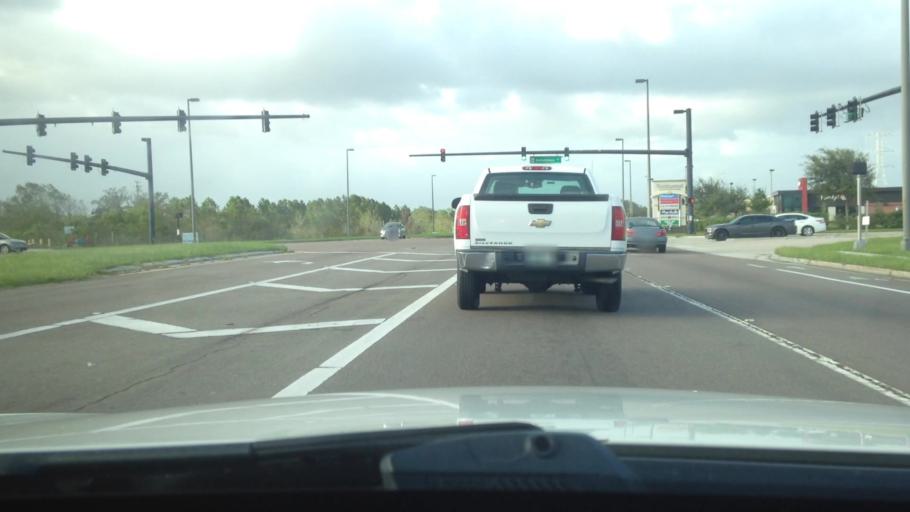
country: US
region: Florida
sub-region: Orange County
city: Conway
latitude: 28.4722
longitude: -81.2900
